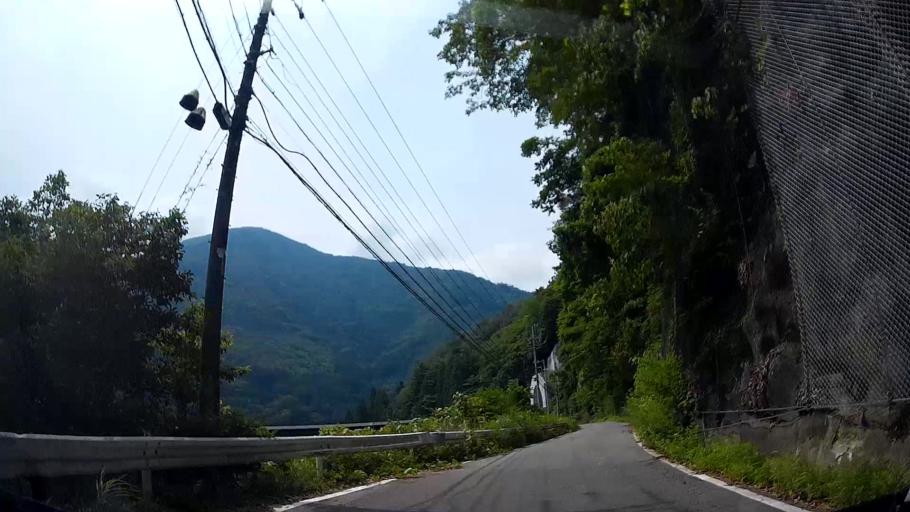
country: JP
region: Nagano
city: Iida
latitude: 35.3363
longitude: 137.9522
